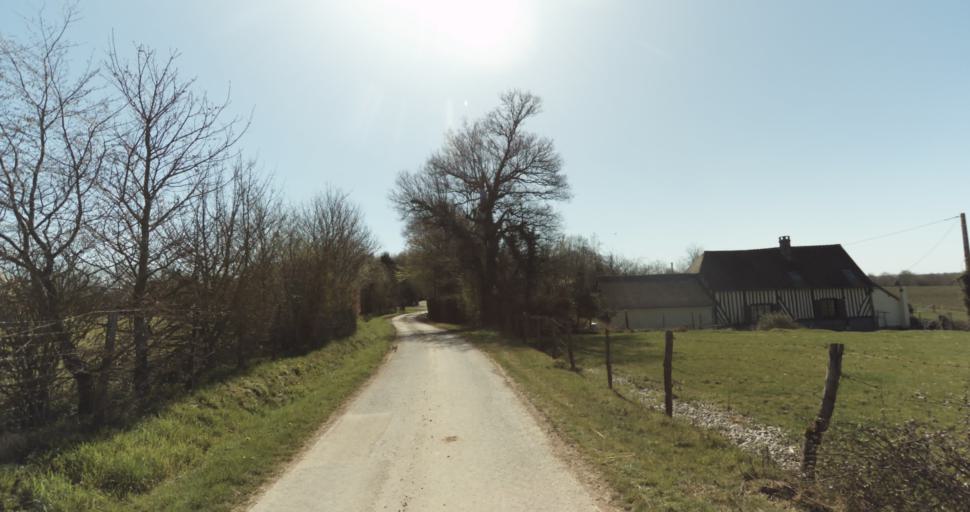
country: FR
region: Lower Normandy
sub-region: Departement du Calvados
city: Livarot
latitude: 49.0201
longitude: 0.1039
